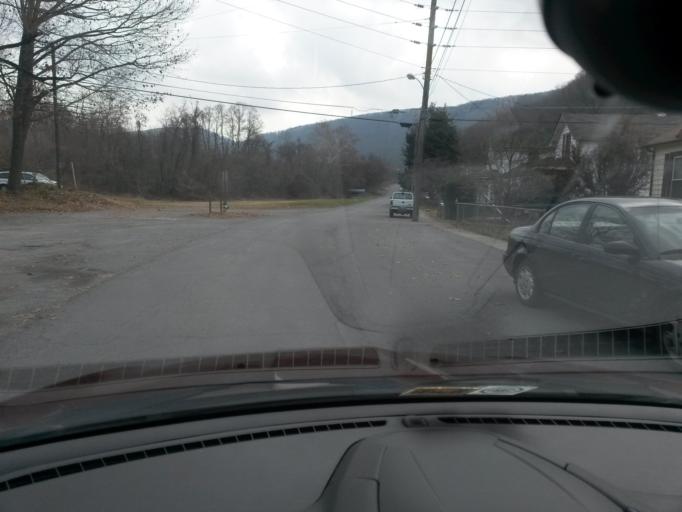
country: US
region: Virginia
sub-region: Alleghany County
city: Clifton Forge
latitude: 37.8133
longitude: -79.8247
